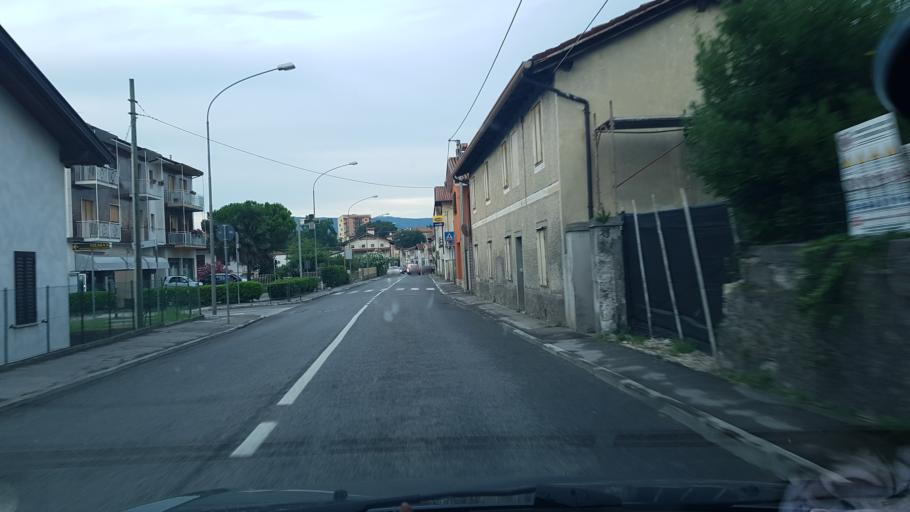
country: IT
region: Friuli Venezia Giulia
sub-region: Provincia di Gorizia
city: Gorizia
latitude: 45.9253
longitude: 13.6037
